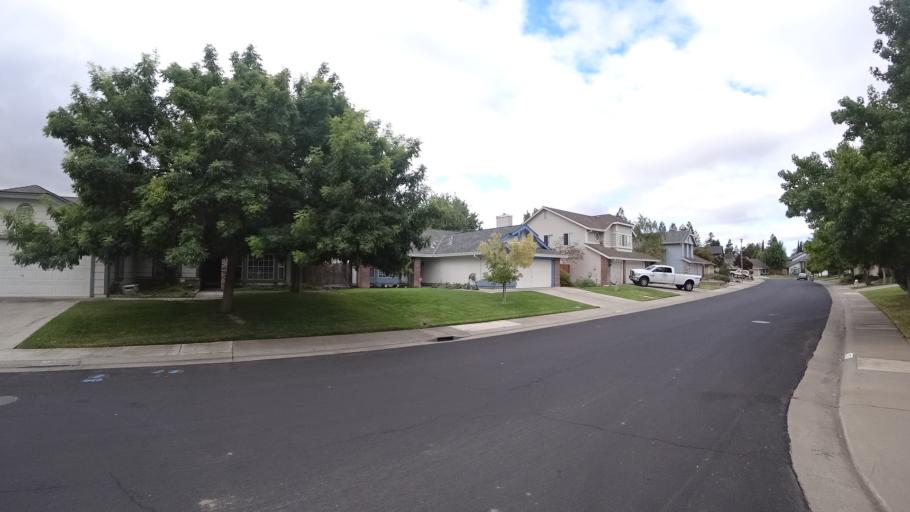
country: US
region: California
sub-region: Sacramento County
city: Laguna
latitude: 38.4123
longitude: -121.4290
